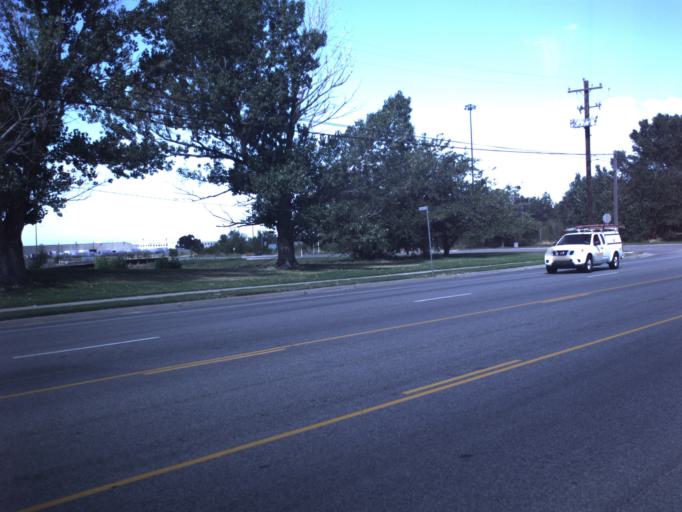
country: US
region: Utah
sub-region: Davis County
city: Clearfield
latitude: 41.0959
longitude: -112.0077
